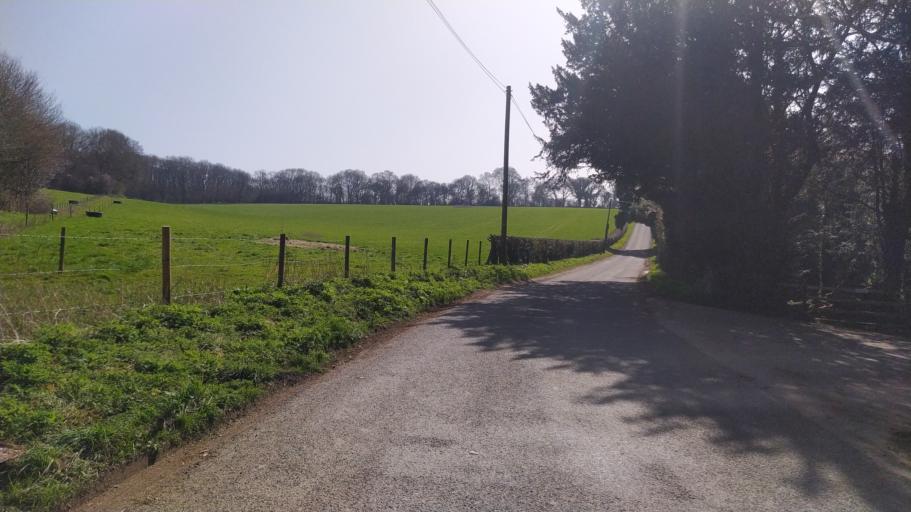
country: GB
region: England
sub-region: Hampshire
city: Kings Worthy
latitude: 51.0694
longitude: -1.2375
